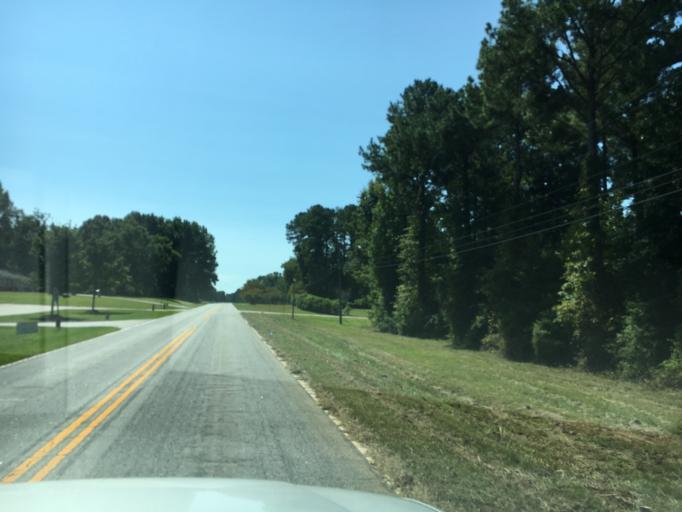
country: US
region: South Carolina
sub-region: Laurens County
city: Clinton
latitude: 34.4420
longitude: -81.8704
